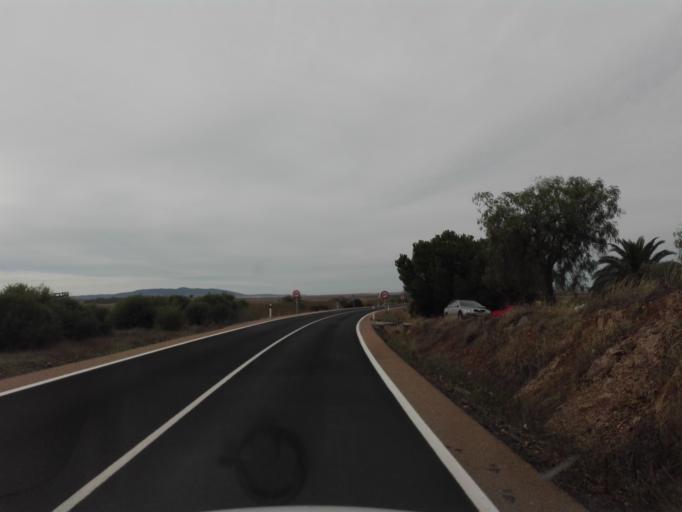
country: ES
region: Extremadura
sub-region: Provincia de Badajoz
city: Valencia de las Torres
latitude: 38.3216
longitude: -5.9638
